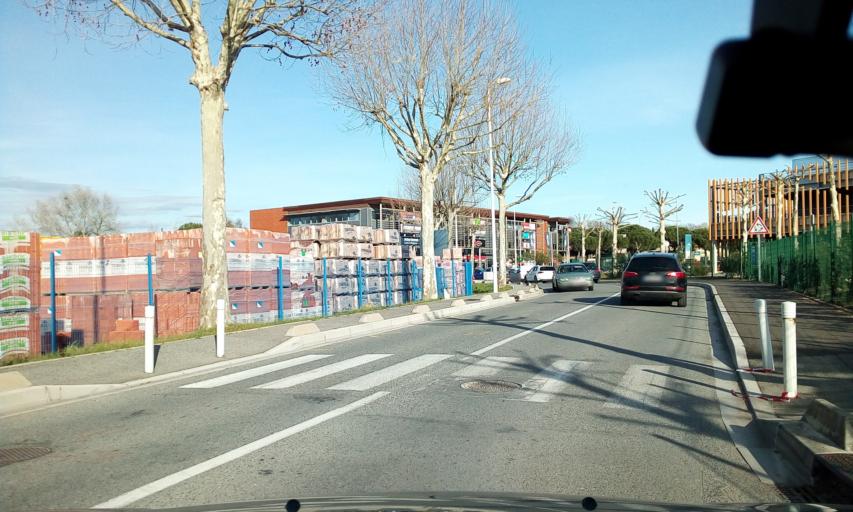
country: FR
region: Provence-Alpes-Cote d'Azur
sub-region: Departement du Var
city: Frejus
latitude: 43.4390
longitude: 6.7198
